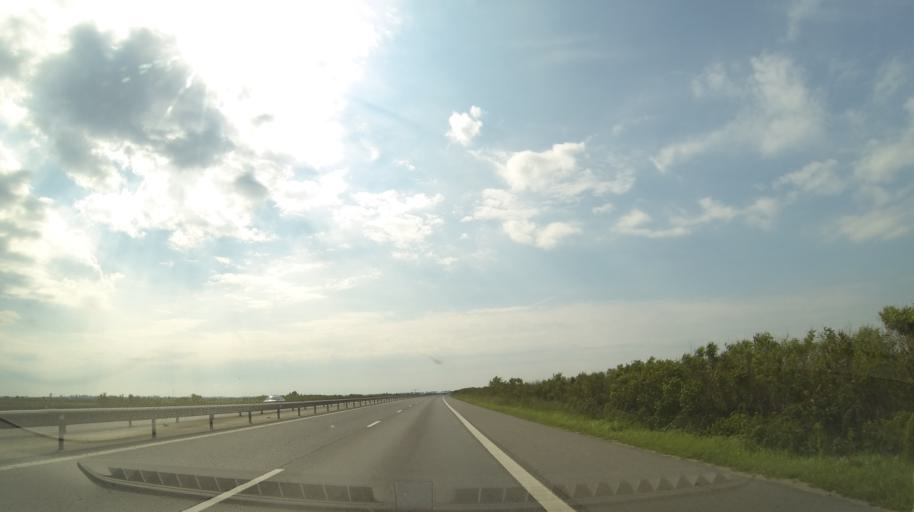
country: RO
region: Dambovita
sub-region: Comuna Corbii Mari
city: Corbii Mari
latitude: 44.5617
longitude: 25.4942
